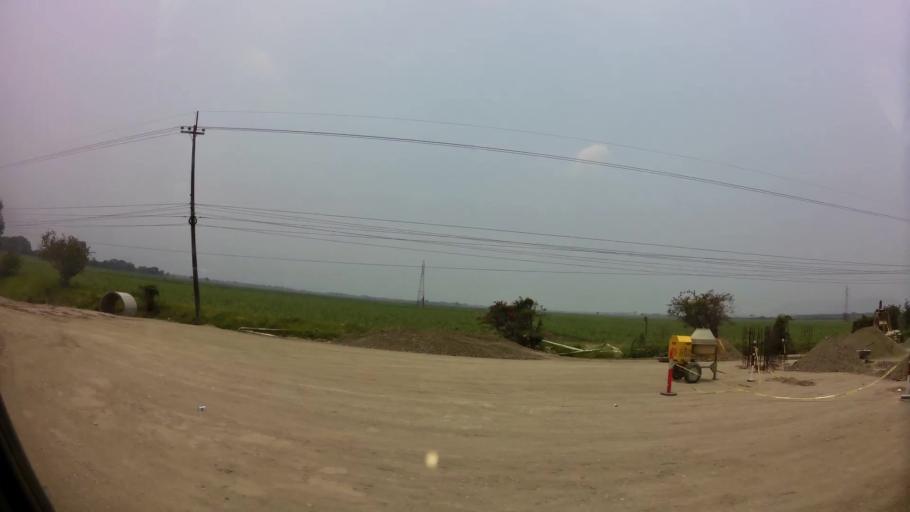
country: HN
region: Yoro
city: El Progreso
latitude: 15.4118
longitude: -87.8535
